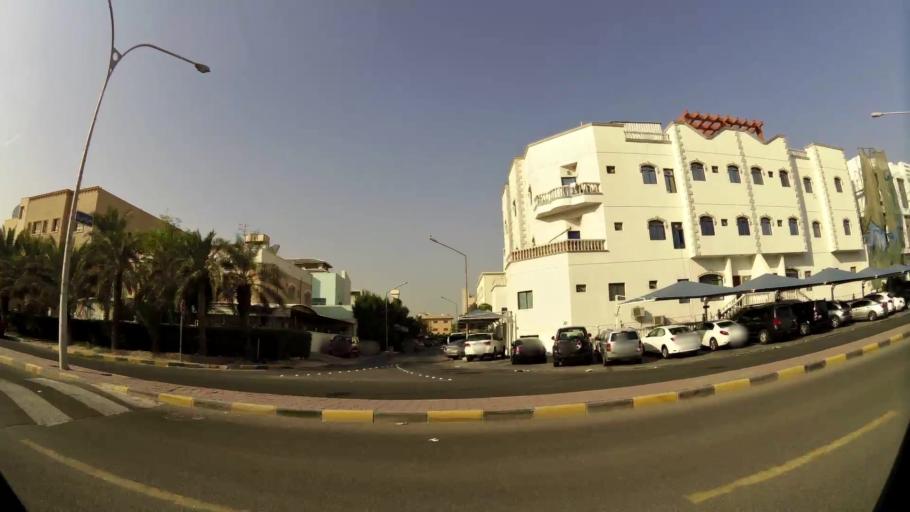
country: KW
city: Bayan
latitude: 29.3156
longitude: 48.0450
